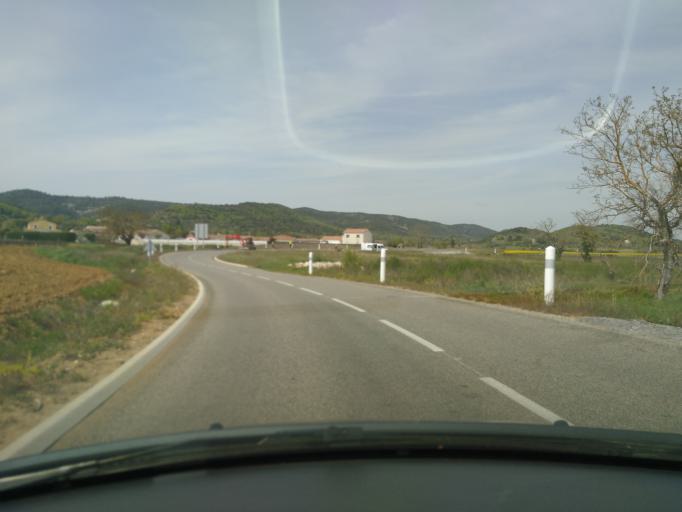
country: FR
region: Rhone-Alpes
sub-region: Departement de l'Ardeche
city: Ruoms
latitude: 44.4100
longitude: 4.4069
